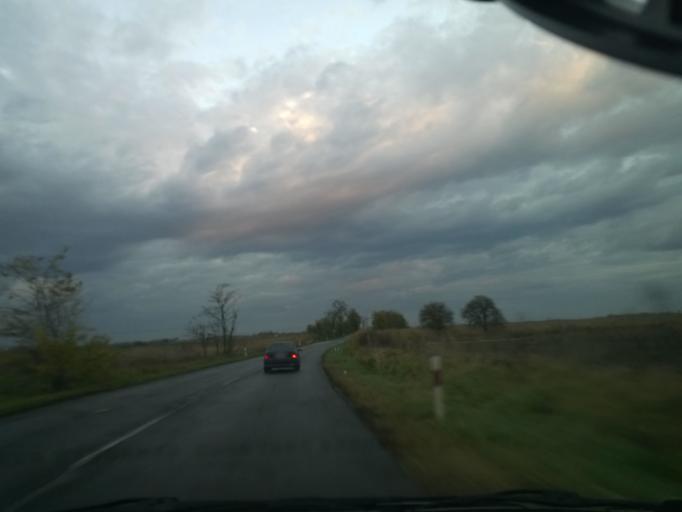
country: HU
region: Bacs-Kiskun
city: Tass
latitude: 47.0396
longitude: 19.0233
